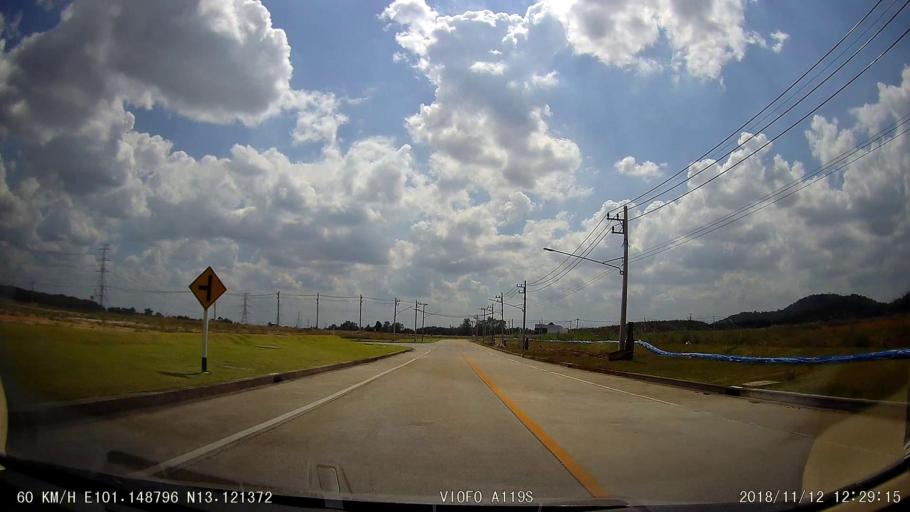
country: TH
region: Chon Buri
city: Ban Talat Bueng
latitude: 13.1210
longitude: 101.1488
